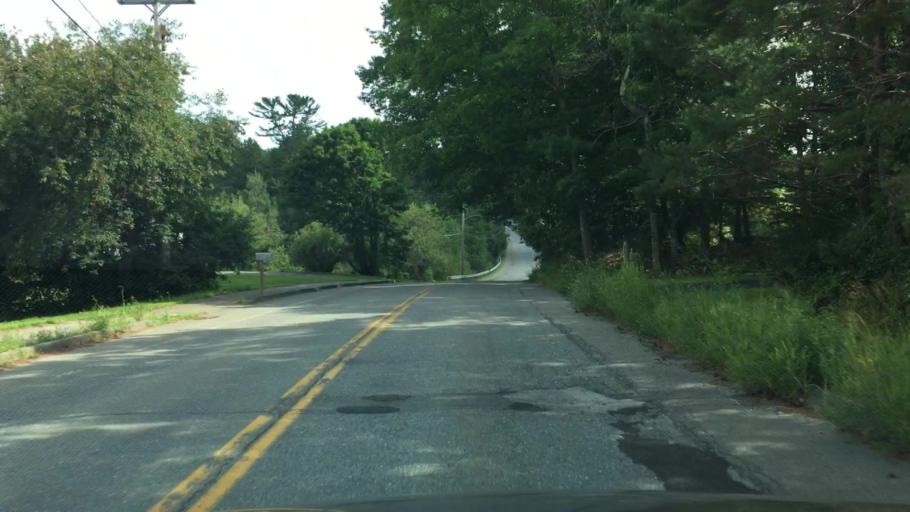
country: US
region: Maine
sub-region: Penobscot County
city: Hampden
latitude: 44.7376
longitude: -68.8606
